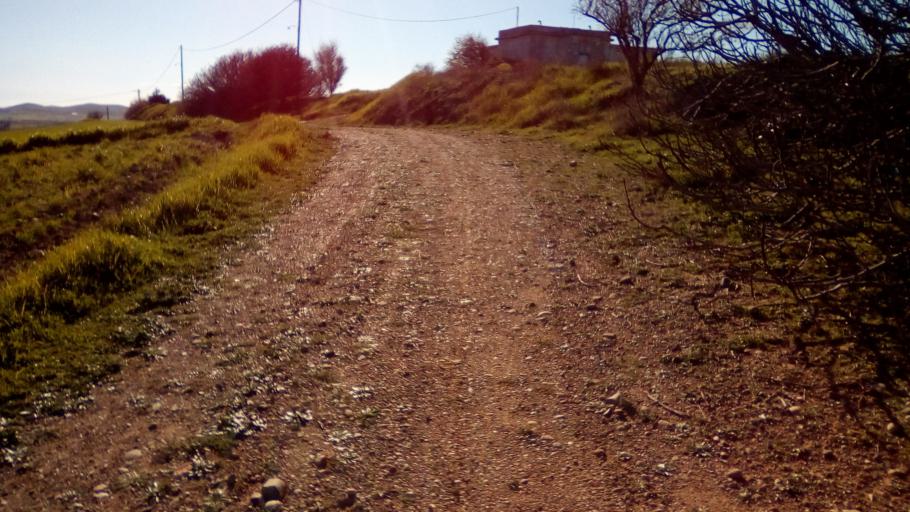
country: GR
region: North Aegean
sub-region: Nomos Lesvou
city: Myrina
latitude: 39.9314
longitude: 25.2363
